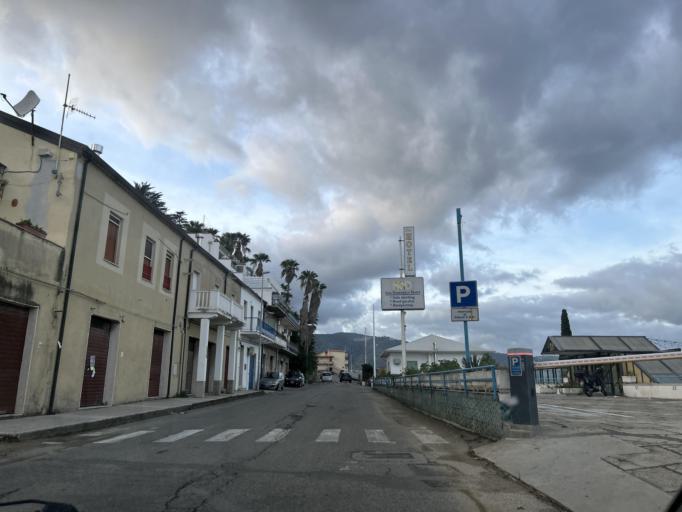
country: IT
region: Calabria
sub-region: Provincia di Catanzaro
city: Soverato Superiore
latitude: 38.6947
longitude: 16.5440
